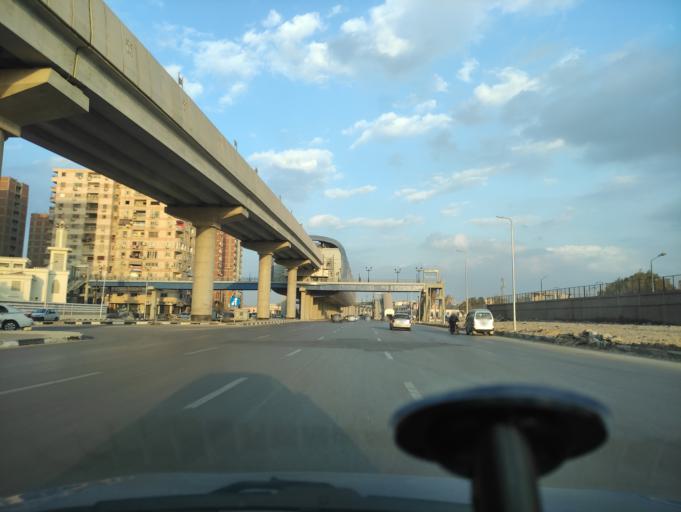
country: EG
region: Muhafazat al Qalyubiyah
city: Al Khankah
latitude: 30.1276
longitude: 31.3584
